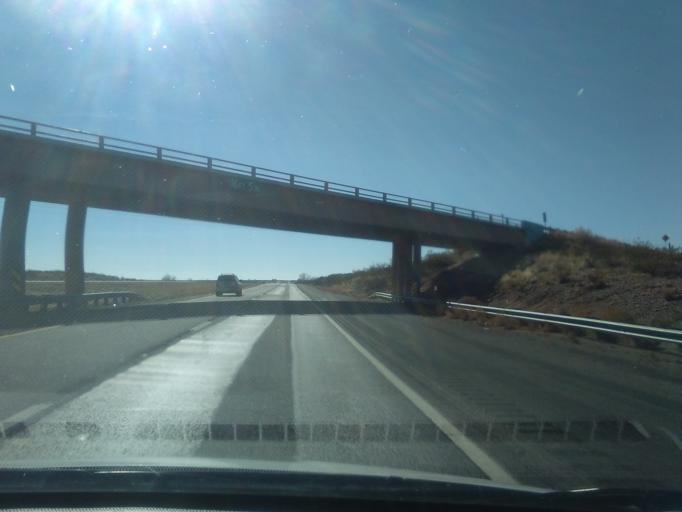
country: US
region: New Mexico
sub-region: Sierra County
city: Elephant Butte
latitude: 33.6071
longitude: -107.1527
